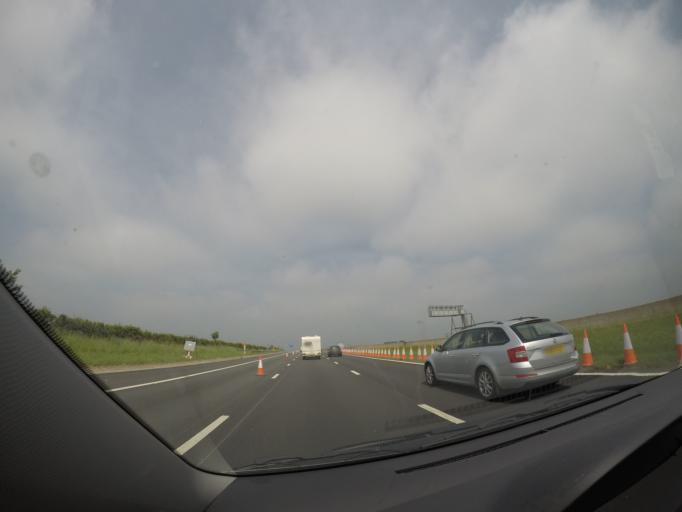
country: GB
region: England
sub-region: North Yorkshire
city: Ripon
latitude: 54.1718
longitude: -1.4523
